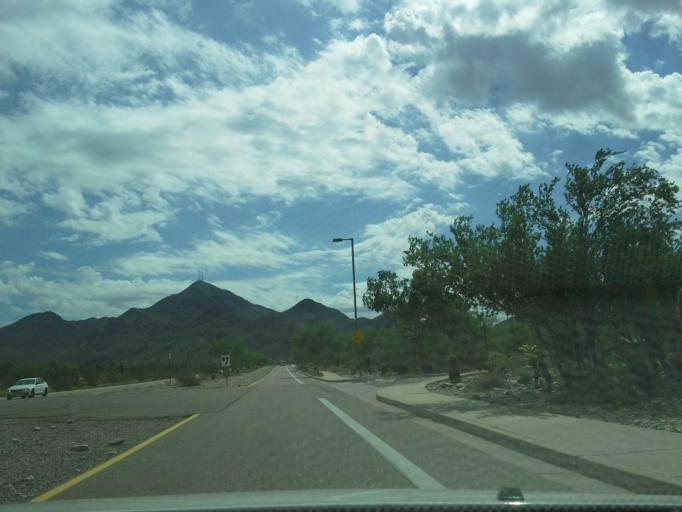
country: US
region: Arizona
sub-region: Maricopa County
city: Scottsdale
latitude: 33.6400
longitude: -111.8573
